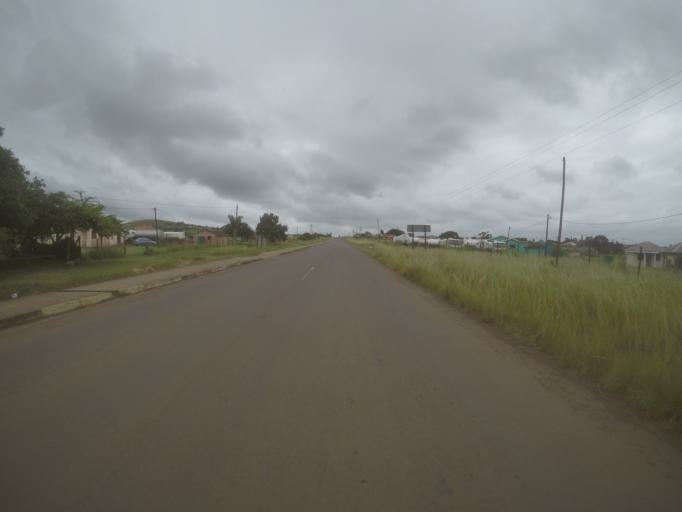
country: ZA
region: KwaZulu-Natal
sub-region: uThungulu District Municipality
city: Empangeni
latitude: -28.7128
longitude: 31.8664
